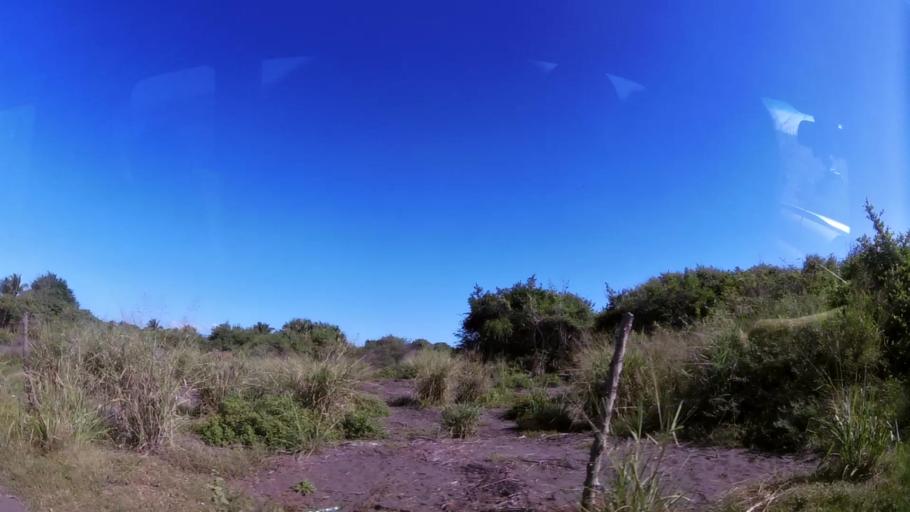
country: GT
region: Jutiapa
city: Pasaco
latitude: 13.8510
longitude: -90.3761
